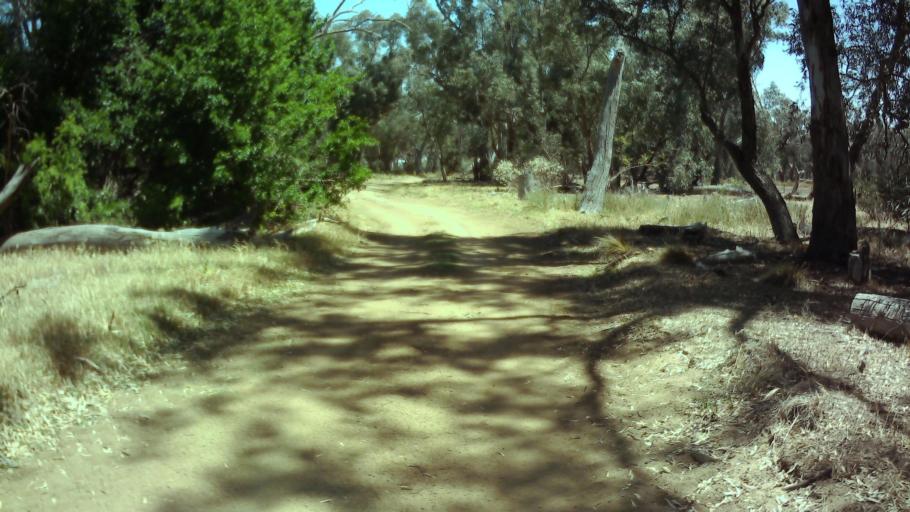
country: AU
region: New South Wales
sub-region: Weddin
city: Grenfell
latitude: -34.0458
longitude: 147.8372
